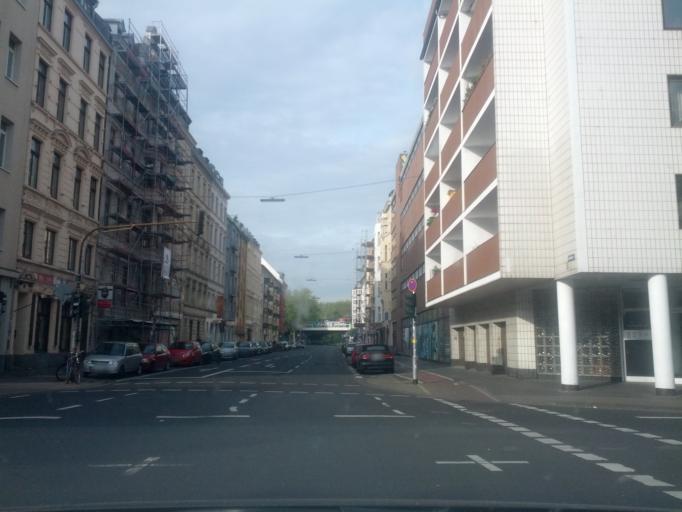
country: DE
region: North Rhine-Westphalia
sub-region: Regierungsbezirk Koln
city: Neustadt/Sued
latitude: 50.9331
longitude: 6.9345
